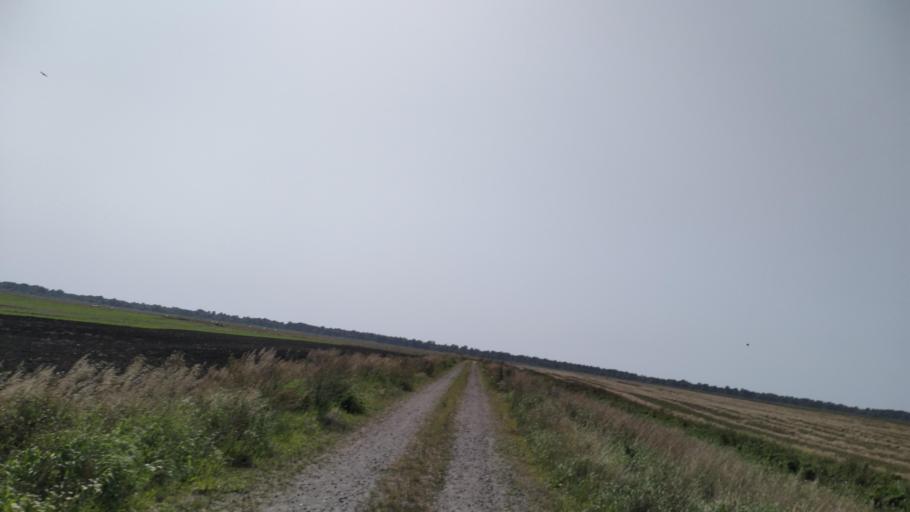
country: BY
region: Brest
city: Davyd-Haradok
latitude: 51.9800
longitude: 27.1633
